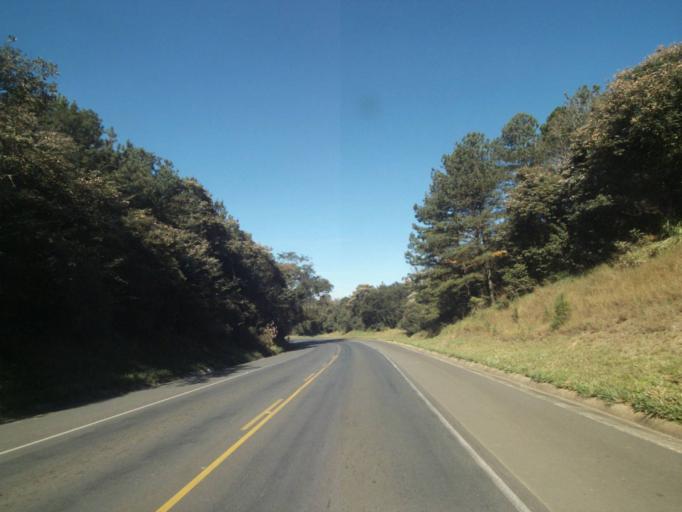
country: BR
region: Parana
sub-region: Tibagi
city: Tibagi
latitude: -24.5089
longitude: -50.4417
